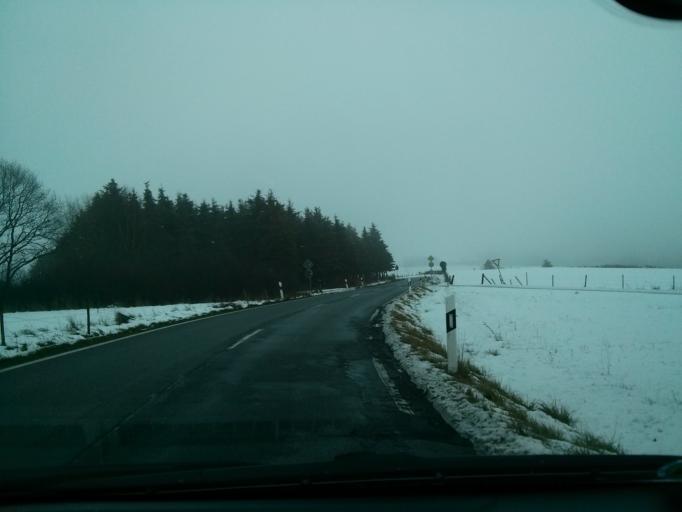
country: DE
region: Rheinland-Pfalz
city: Berg
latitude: 50.5672
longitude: 6.9554
